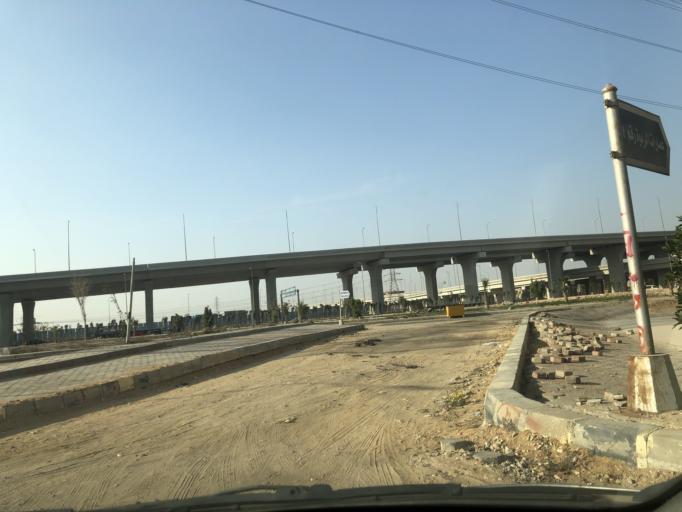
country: EG
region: Al Jizah
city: Madinat Sittah Uktubar
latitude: 29.9092
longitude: 30.9303
